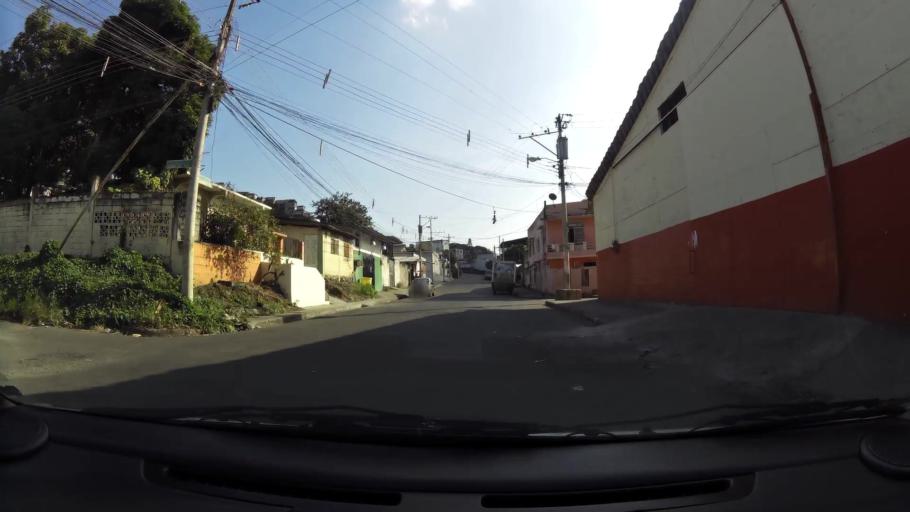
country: EC
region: Guayas
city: Guayaquil
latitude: -2.1419
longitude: -79.9286
